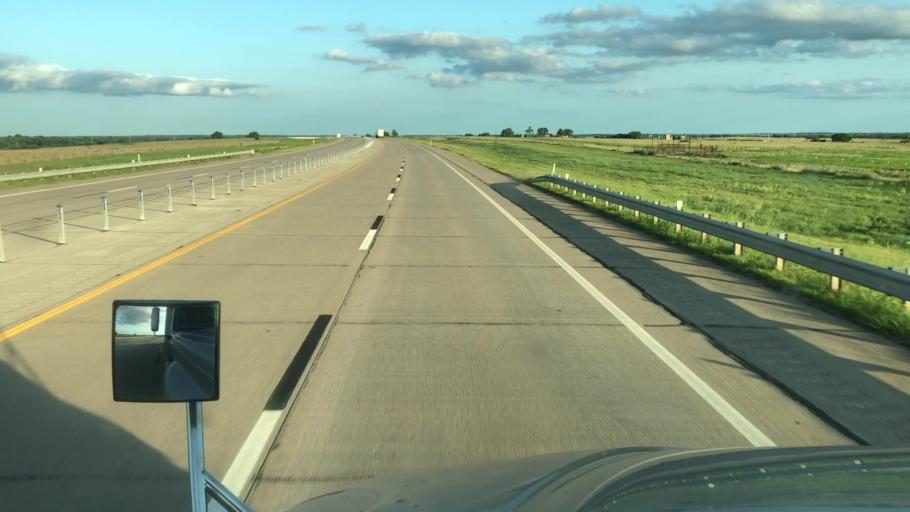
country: US
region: Oklahoma
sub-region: Pawnee County
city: Pawnee
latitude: 36.3410
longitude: -97.0239
